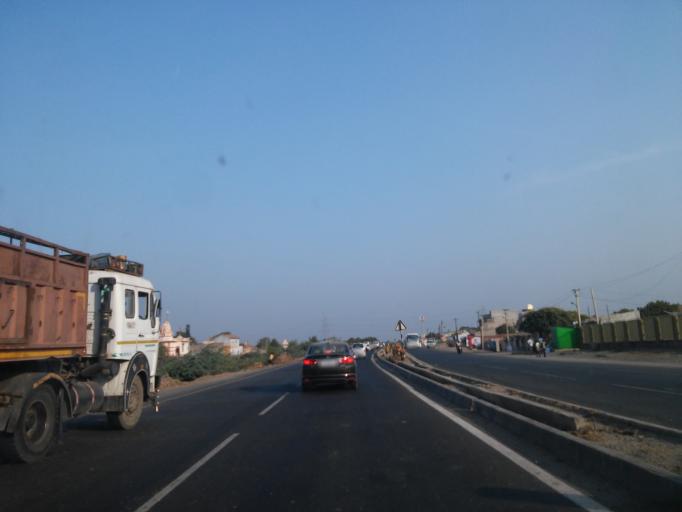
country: IN
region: Gujarat
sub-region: Ahmadabad
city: Mandal
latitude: 23.0969
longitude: 72.1087
